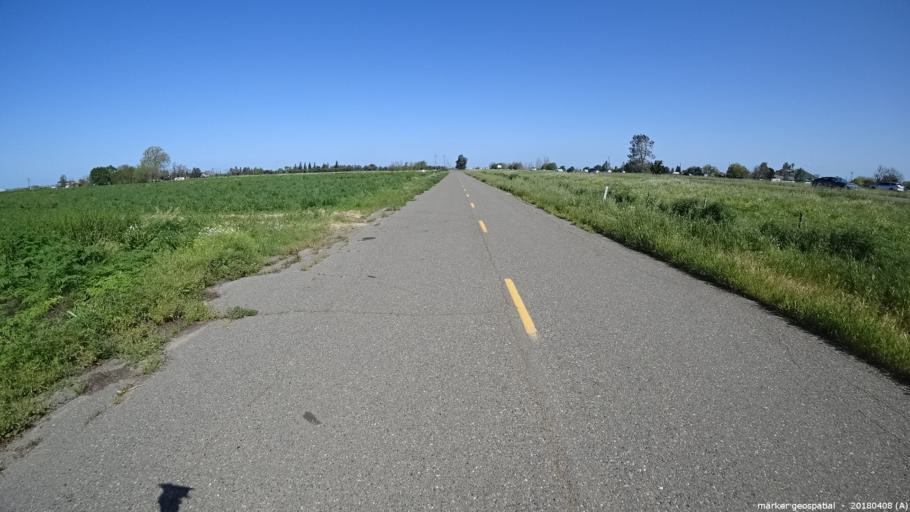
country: US
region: California
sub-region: Sacramento County
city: Walnut Grove
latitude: 38.3293
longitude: -121.4678
